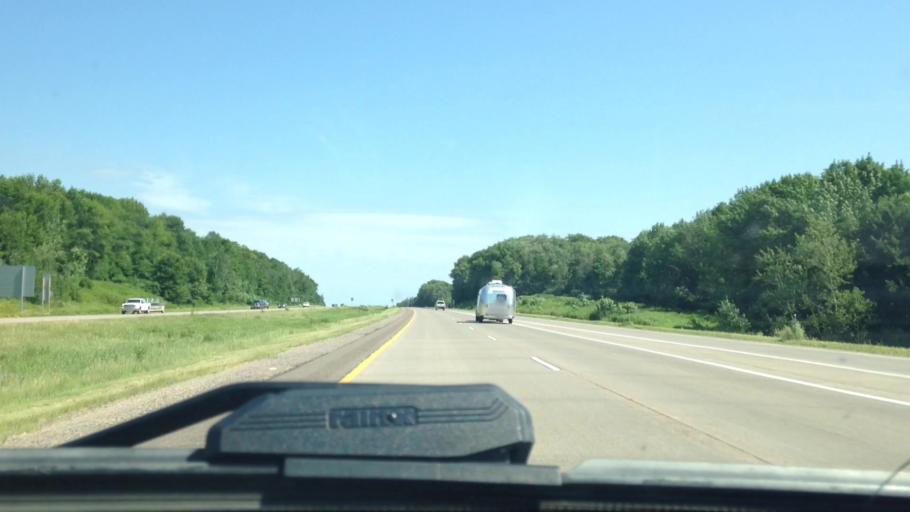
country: US
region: Wisconsin
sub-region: Barron County
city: Rice Lake
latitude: 45.5138
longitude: -91.7606
